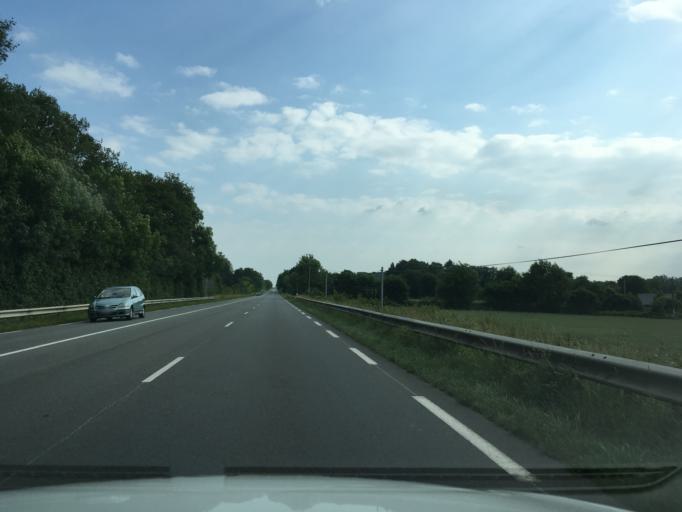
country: FR
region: Poitou-Charentes
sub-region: Departement des Deux-Sevres
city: Le Tallud
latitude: 46.6106
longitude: -0.2851
